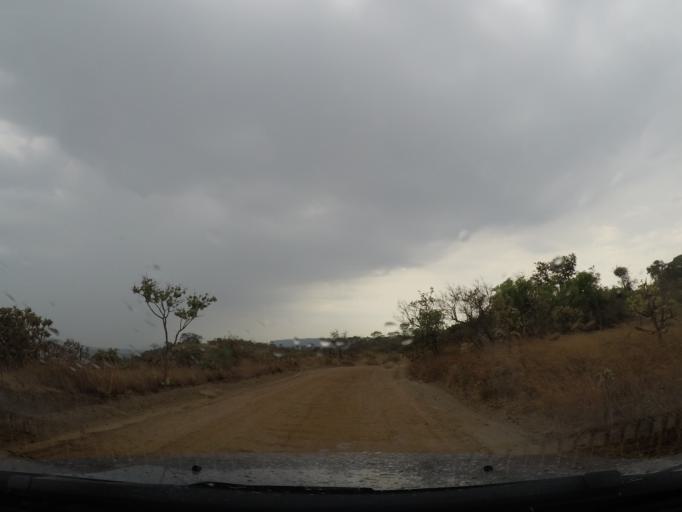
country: BR
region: Goias
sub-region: Pirenopolis
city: Pirenopolis
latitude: -15.8272
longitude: -48.9047
